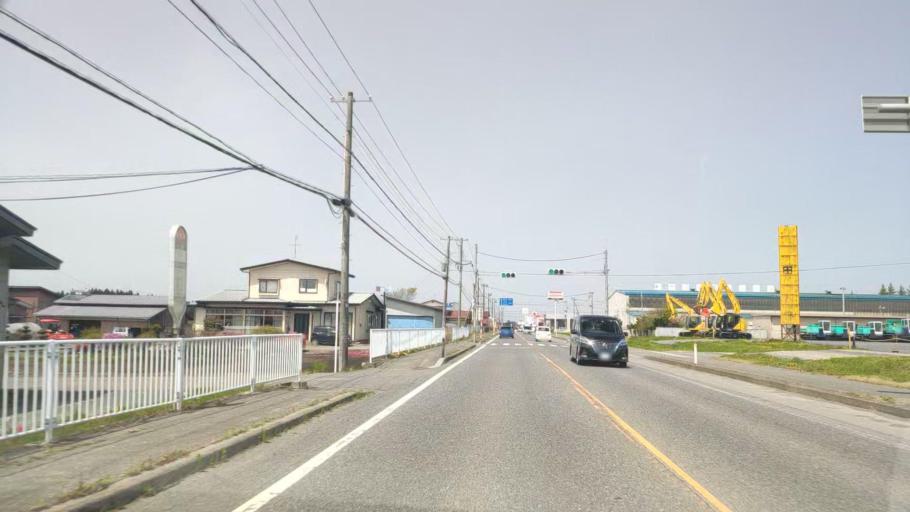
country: JP
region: Aomori
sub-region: Misawa Shi
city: Inuotose
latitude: 40.6476
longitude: 141.1973
